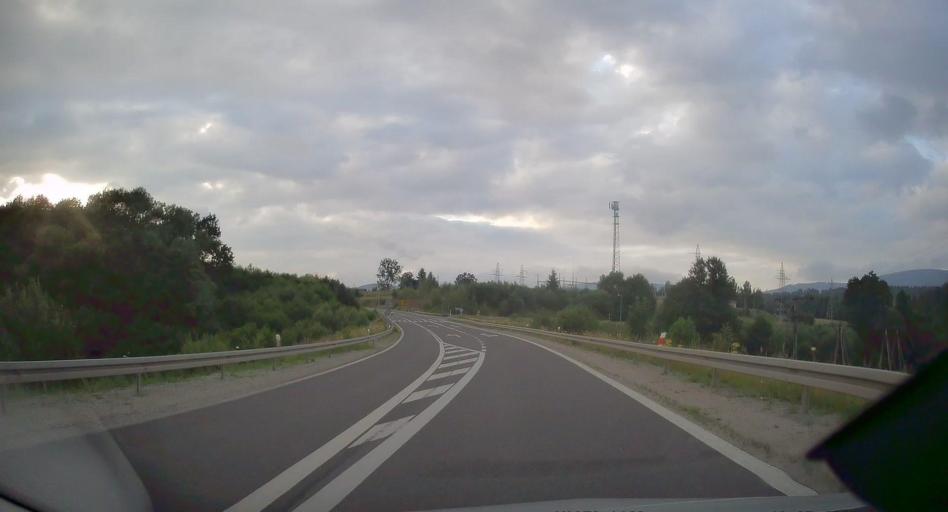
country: PL
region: Lower Silesian Voivodeship
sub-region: Powiat klodzki
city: Nowa Ruda
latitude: 50.5957
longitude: 16.5197
